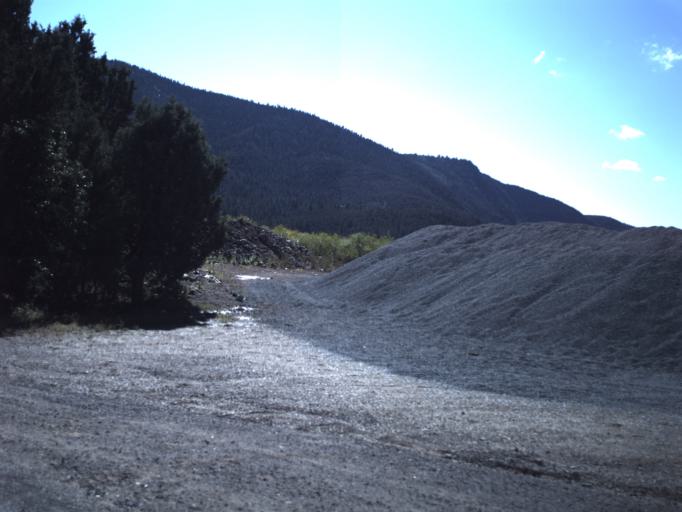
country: US
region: Utah
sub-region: Beaver County
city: Beaver
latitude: 38.2693
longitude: -112.4872
